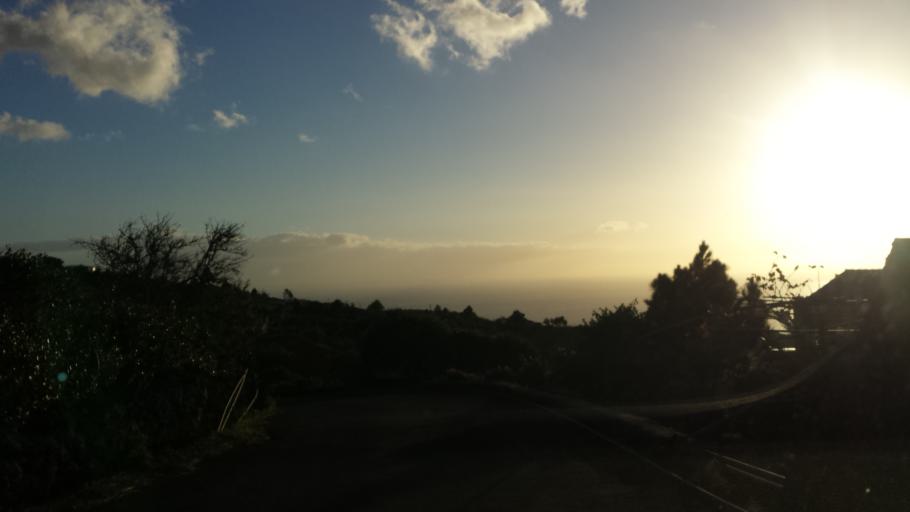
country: ES
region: Canary Islands
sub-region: Provincia de Santa Cruz de Tenerife
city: El Paso
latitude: 28.6143
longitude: -17.8909
